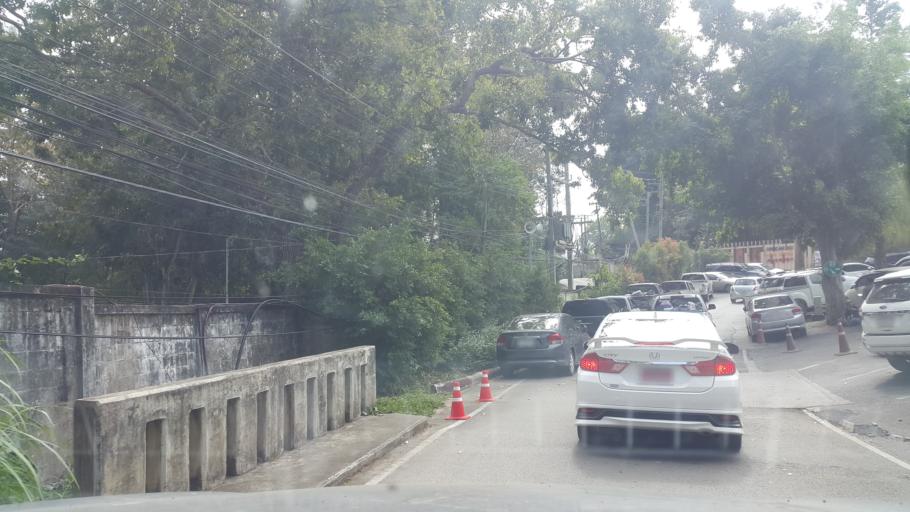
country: TH
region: Chiang Mai
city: Chiang Mai
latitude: 18.8068
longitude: 98.9473
